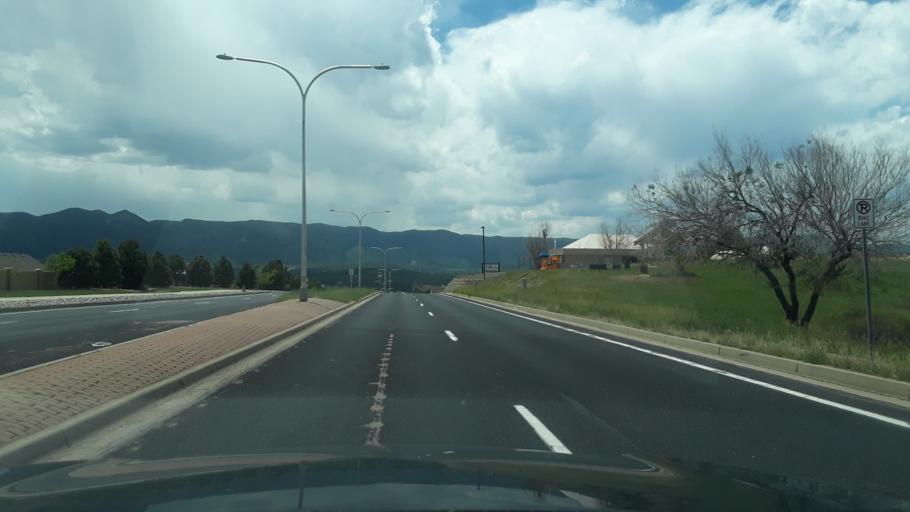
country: US
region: Colorado
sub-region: El Paso County
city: Gleneagle
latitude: 39.0273
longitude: -104.8094
